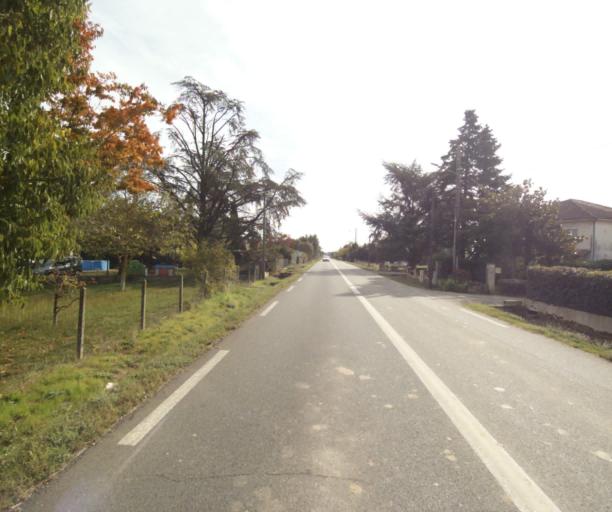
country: FR
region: Midi-Pyrenees
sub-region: Departement du Tarn-et-Garonne
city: Labastide-Saint-Pierre
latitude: 43.9241
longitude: 1.3908
